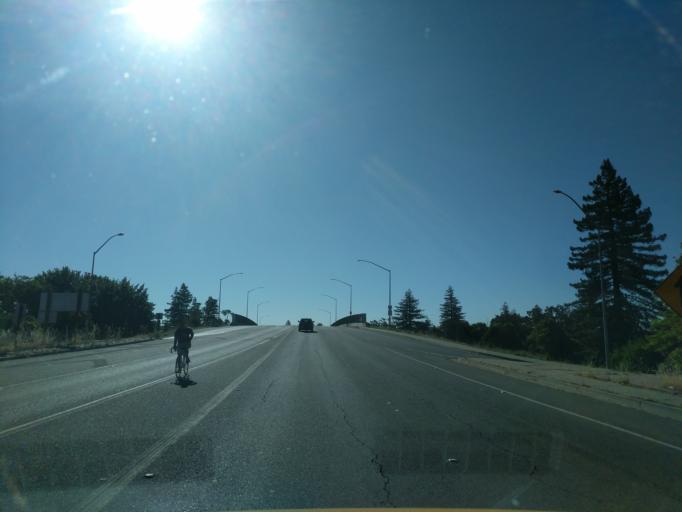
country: US
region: California
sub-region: Yolo County
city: Davis
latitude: 38.5404
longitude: -121.7373
